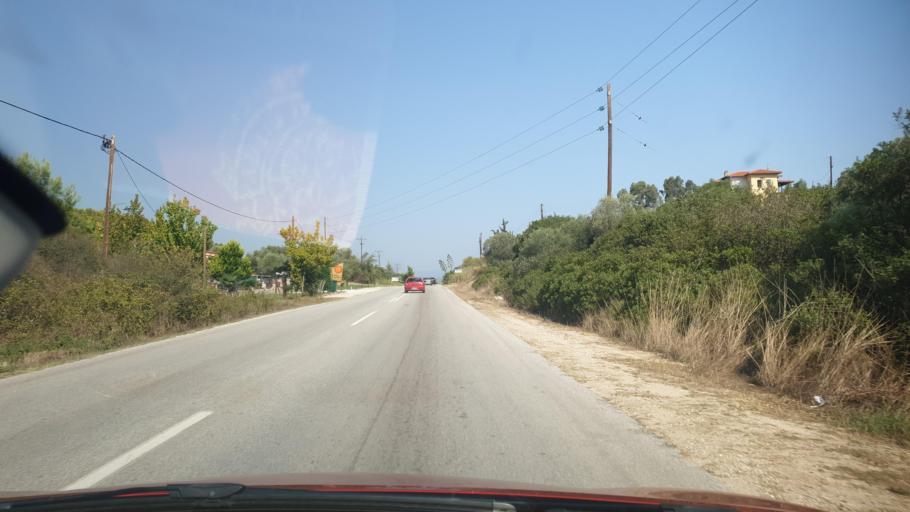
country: GR
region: Central Macedonia
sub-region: Nomos Chalkidikis
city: Agios Nikolaos
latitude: 40.2224
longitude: 23.7467
